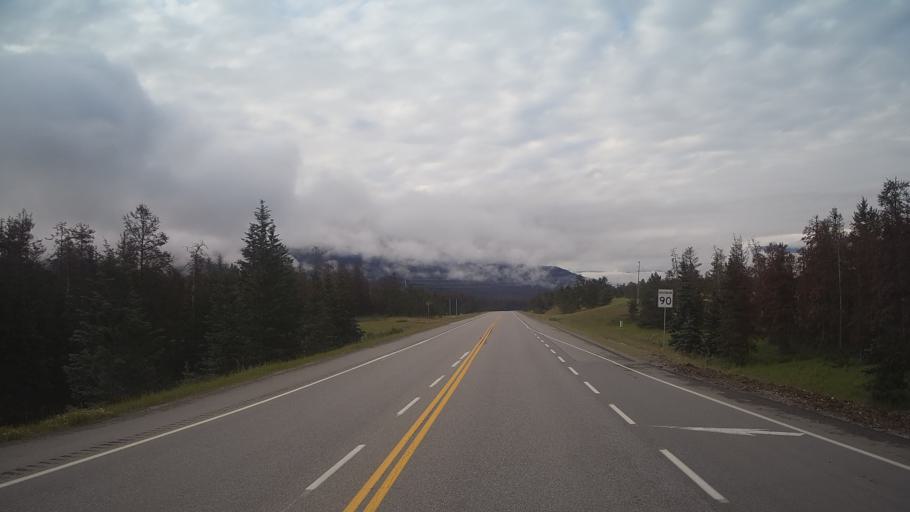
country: CA
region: Alberta
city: Jasper Park Lodge
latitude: 52.9379
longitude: -118.0392
